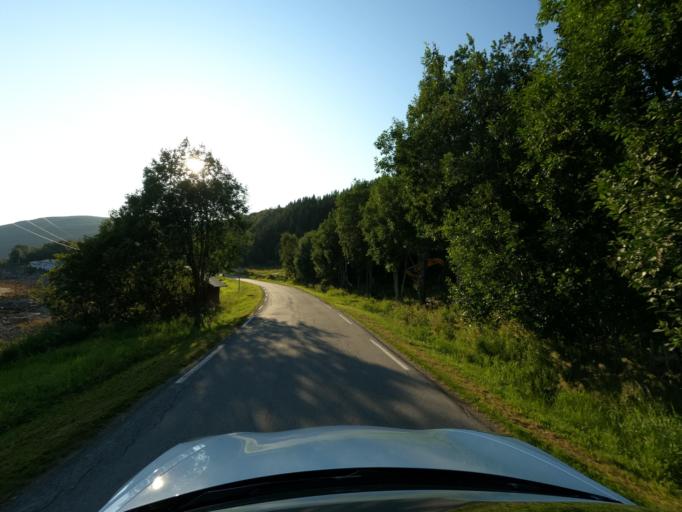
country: NO
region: Nordland
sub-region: Ballangen
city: Ballangen
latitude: 68.4682
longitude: 16.8104
